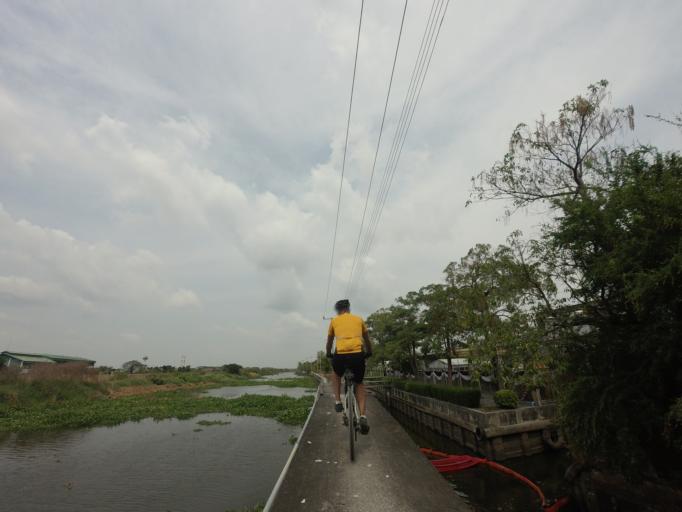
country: TH
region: Bangkok
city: Lat Krabang
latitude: 13.6881
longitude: 100.7712
